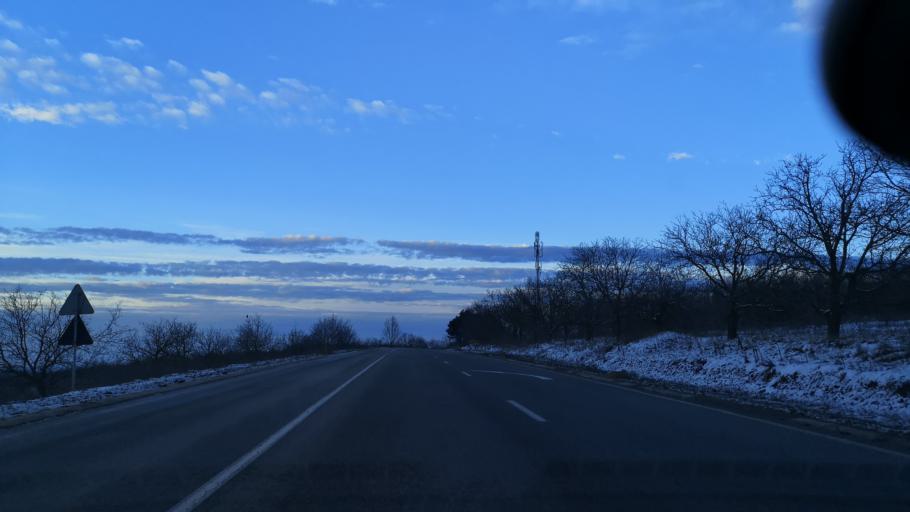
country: MD
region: Orhei
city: Orhei
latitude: 47.5329
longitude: 28.7940
